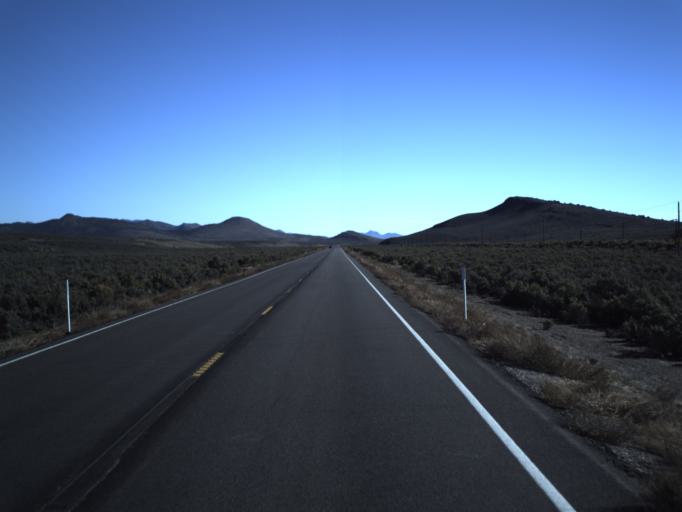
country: US
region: Utah
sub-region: Washington County
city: Enterprise
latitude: 37.7656
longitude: -113.9828
